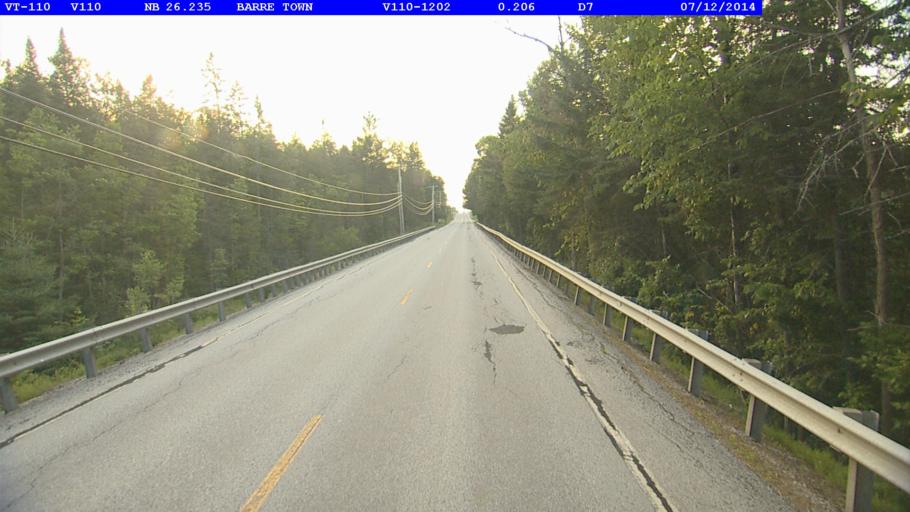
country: US
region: Vermont
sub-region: Washington County
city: South Barre
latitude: 44.1510
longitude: -72.4409
